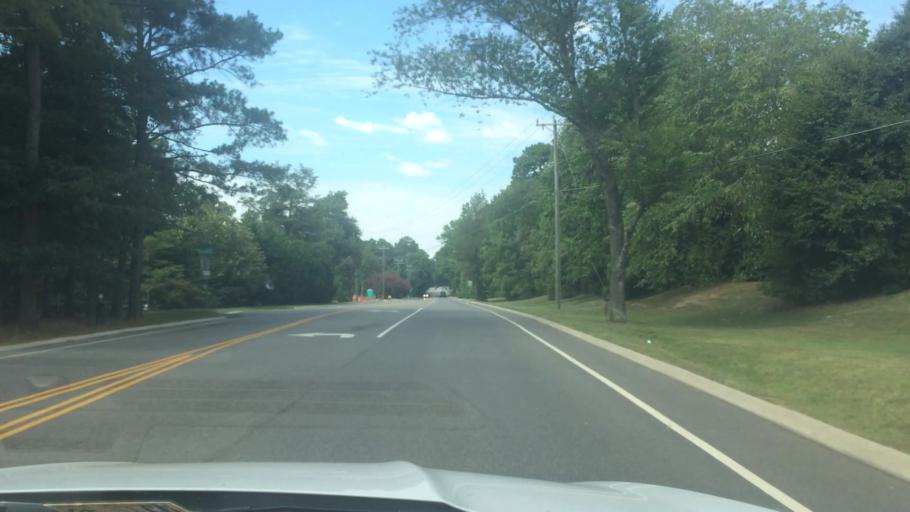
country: US
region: Virginia
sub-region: York County
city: Yorktown
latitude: 37.1557
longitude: -76.4459
